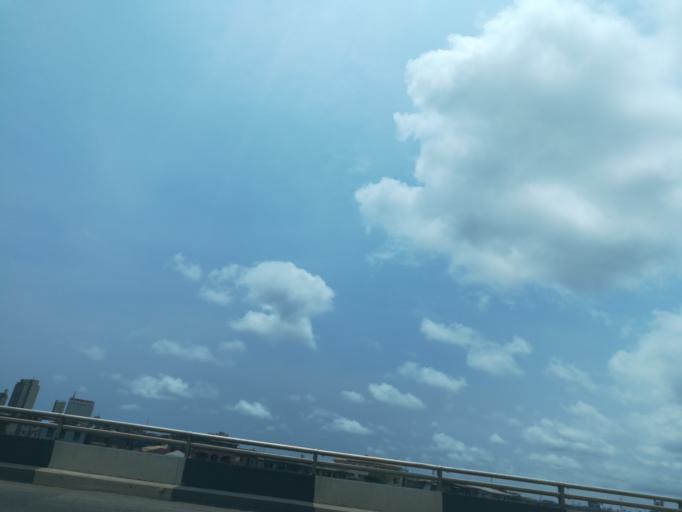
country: NG
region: Lagos
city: Lagos
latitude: 6.4657
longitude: 3.3922
